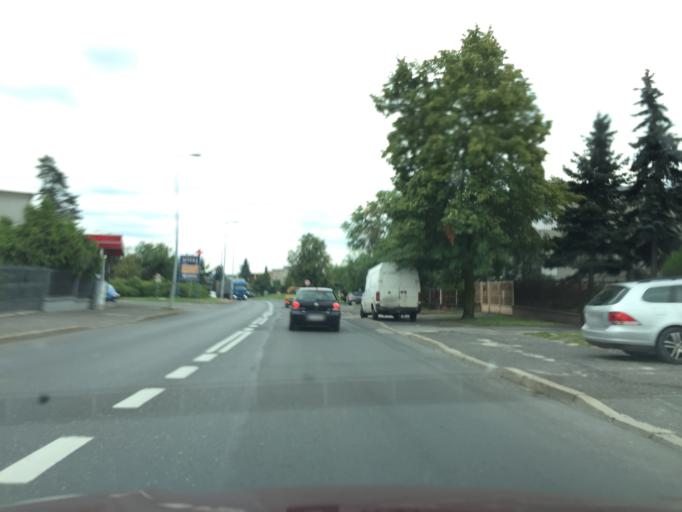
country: PL
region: Greater Poland Voivodeship
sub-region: Kalisz
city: Kalisz
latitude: 51.7750
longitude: 18.0890
